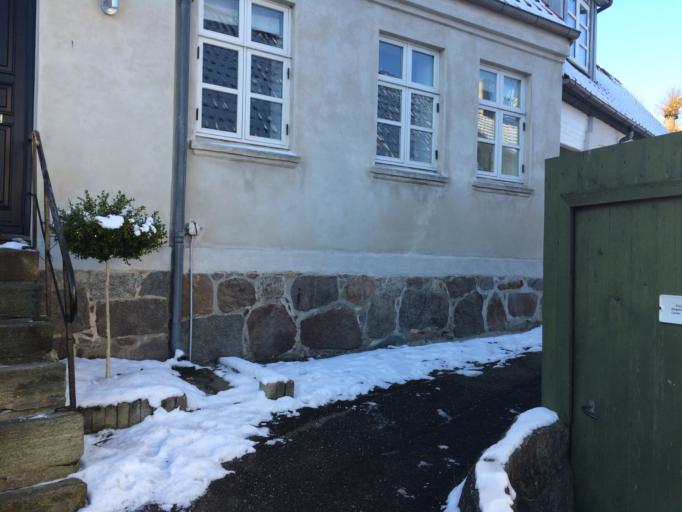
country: DK
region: Zealand
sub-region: Roskilde Kommune
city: Roskilde
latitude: 55.6491
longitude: 12.0771
